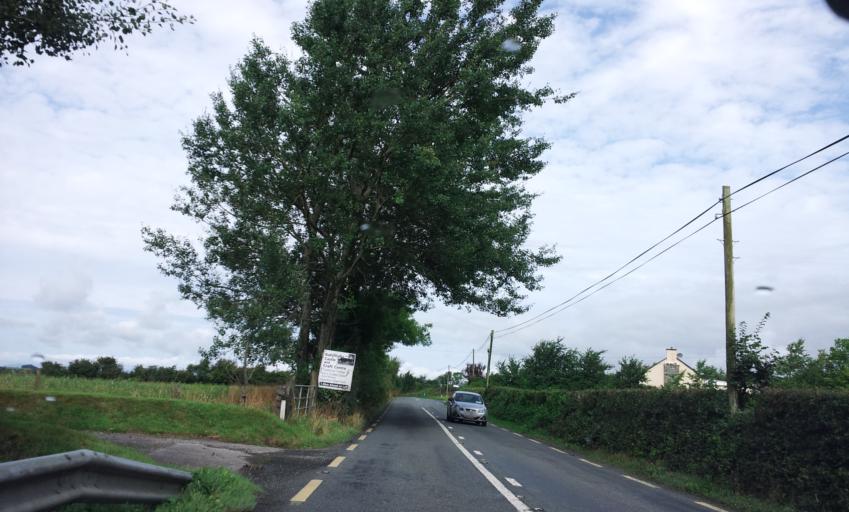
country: IE
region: Munster
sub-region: Ciarrai
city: Killorglin
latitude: 52.0809
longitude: -9.6635
